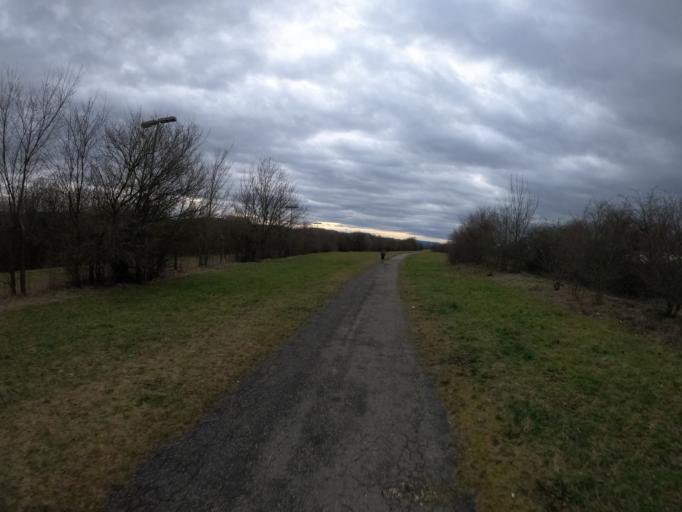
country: DE
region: Baden-Wuerttemberg
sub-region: Regierungsbezirk Stuttgart
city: Eislingen
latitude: 48.7070
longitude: 9.6939
